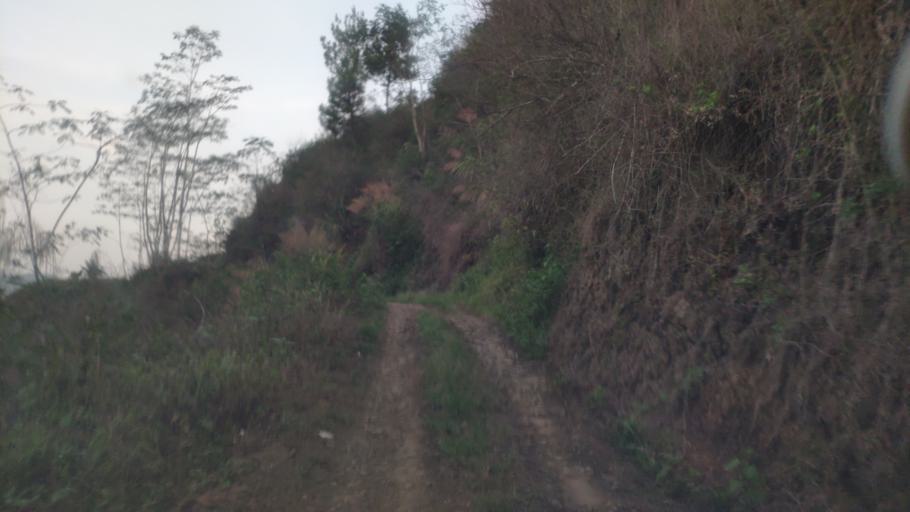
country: ID
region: Central Java
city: Buaran
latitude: -7.2639
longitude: 109.5770
